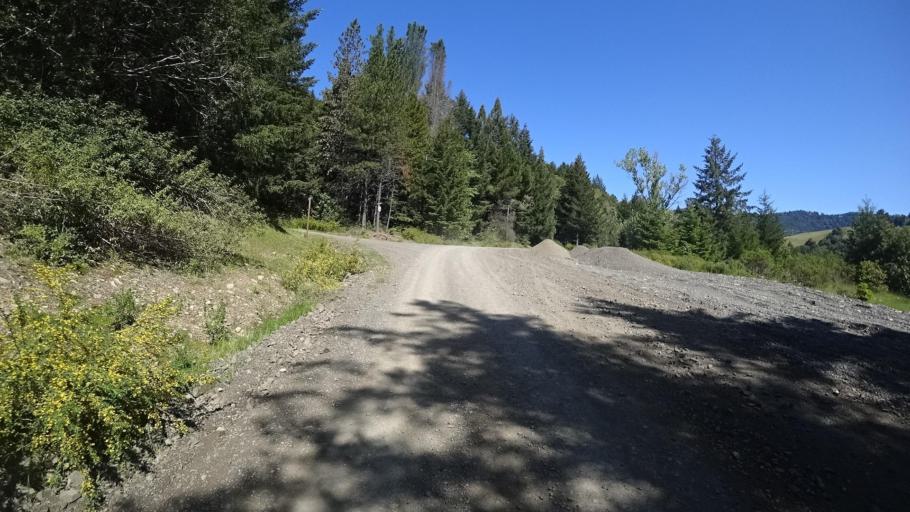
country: US
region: California
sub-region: Humboldt County
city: Rio Dell
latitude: 40.2247
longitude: -124.1115
